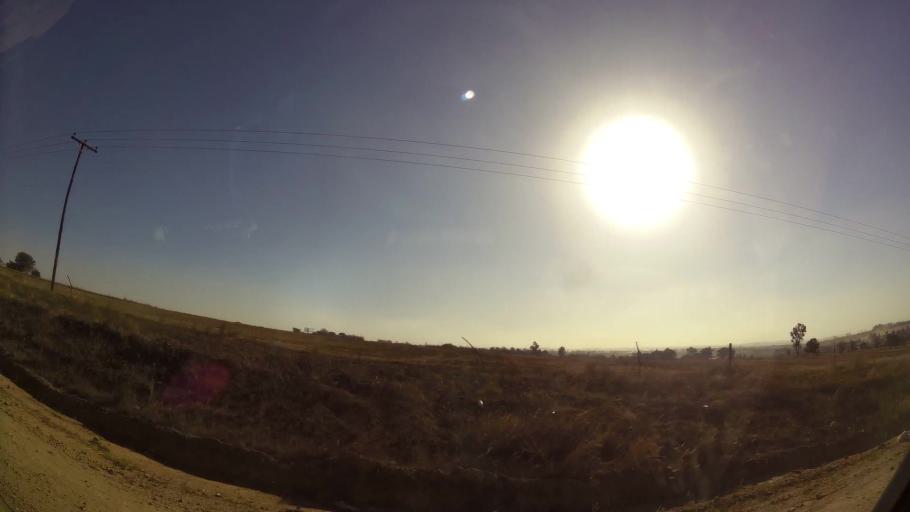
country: ZA
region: Gauteng
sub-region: City of Johannesburg Metropolitan Municipality
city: Diepsloot
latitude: -25.9568
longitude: 27.9586
